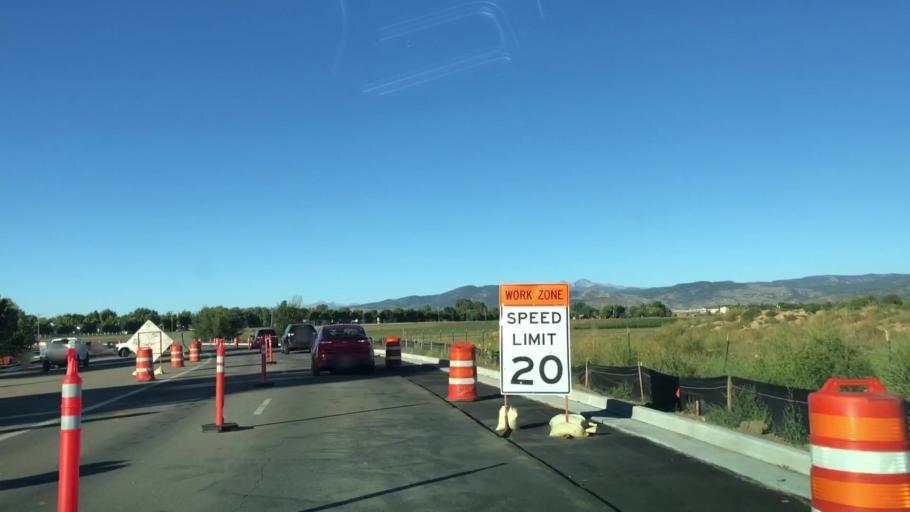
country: US
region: Colorado
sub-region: Larimer County
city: Loveland
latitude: 40.3956
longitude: -105.1144
